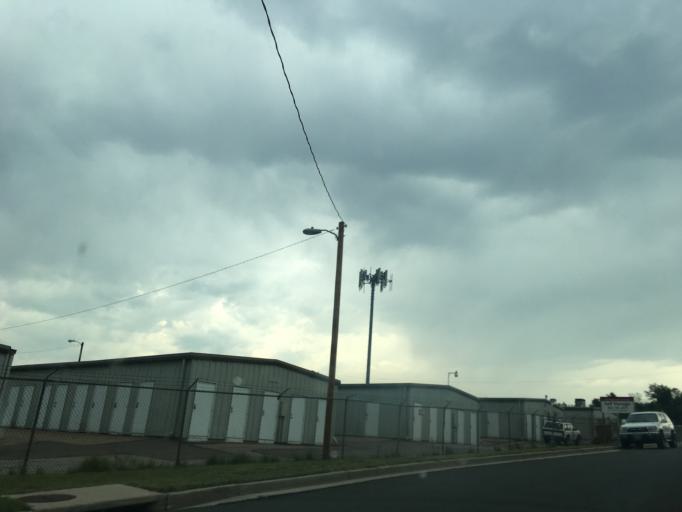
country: US
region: Colorado
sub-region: Arapahoe County
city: Sheridan
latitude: 39.6544
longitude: -105.0298
